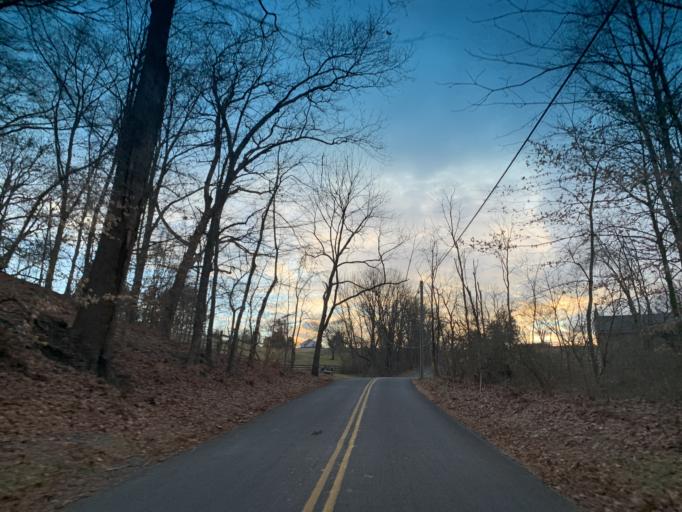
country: US
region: Maryland
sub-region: Harford County
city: Bel Air North
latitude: 39.6211
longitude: -76.3094
